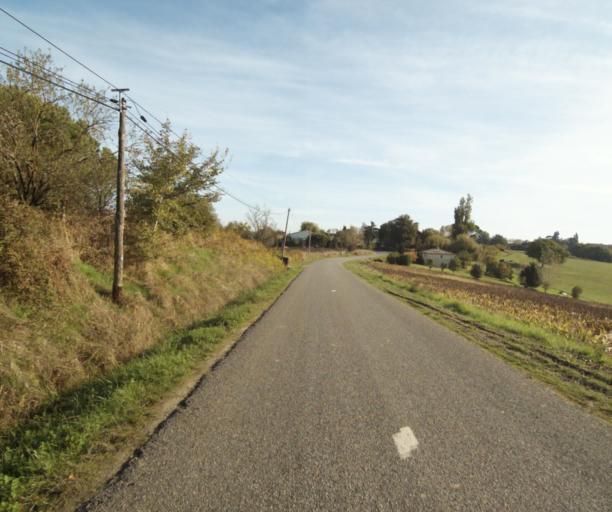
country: FR
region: Midi-Pyrenees
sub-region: Departement de la Haute-Garonne
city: Villemur-sur-Tarn
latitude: 43.9016
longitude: 1.4867
